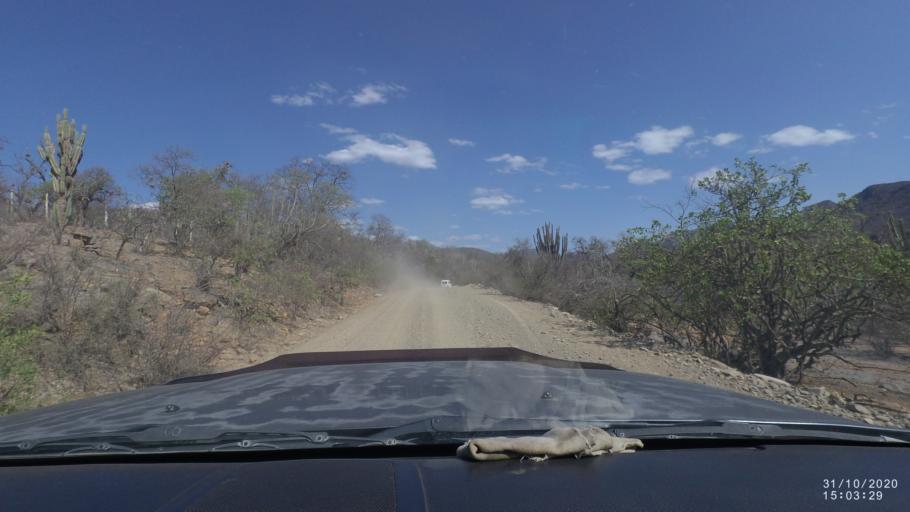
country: BO
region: Cochabamba
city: Aiquile
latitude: -18.2757
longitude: -64.8063
